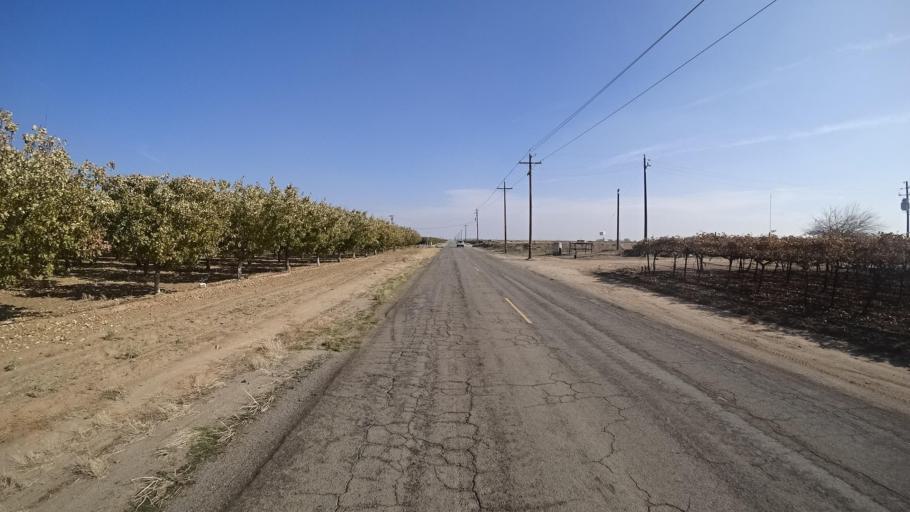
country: US
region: California
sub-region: Kern County
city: Greenacres
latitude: 35.5299
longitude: -119.1261
